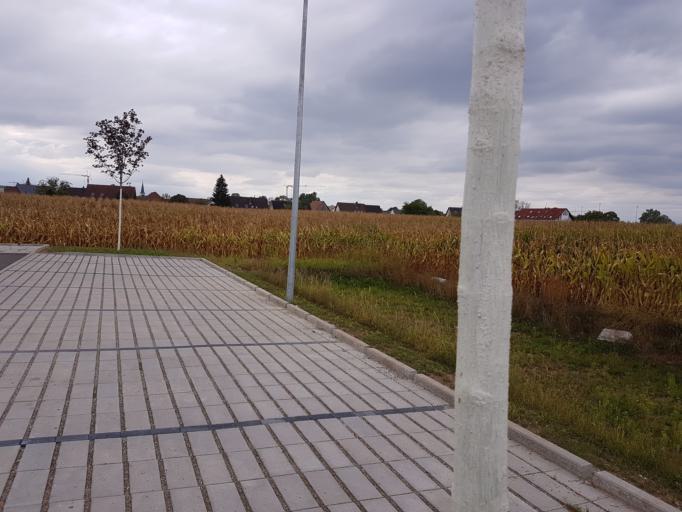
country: DE
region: Baden-Wuerttemberg
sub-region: Freiburg Region
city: Merdingen
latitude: 47.9832
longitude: 7.6661
